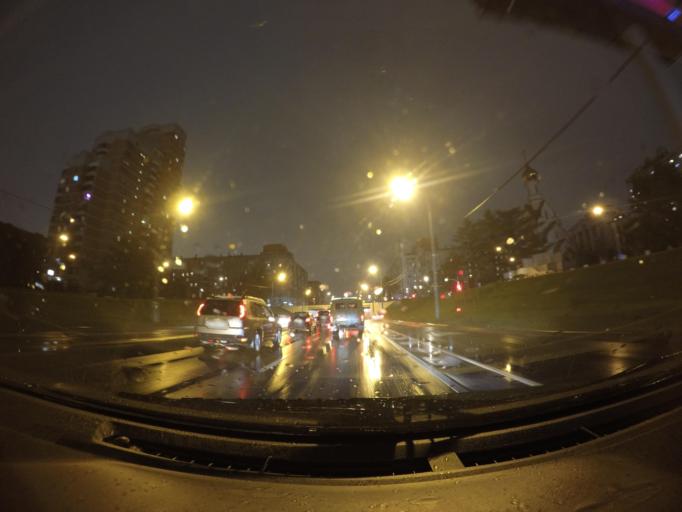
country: RU
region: Moskovskaya
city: Kozhukhovo
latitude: 55.7018
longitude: 37.6675
